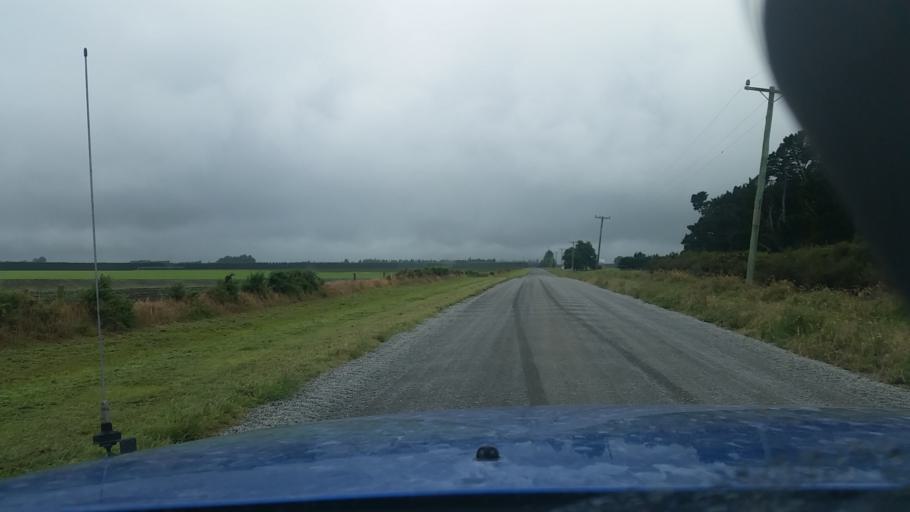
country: NZ
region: Canterbury
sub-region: Ashburton District
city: Methven
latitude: -43.6631
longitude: 171.7841
